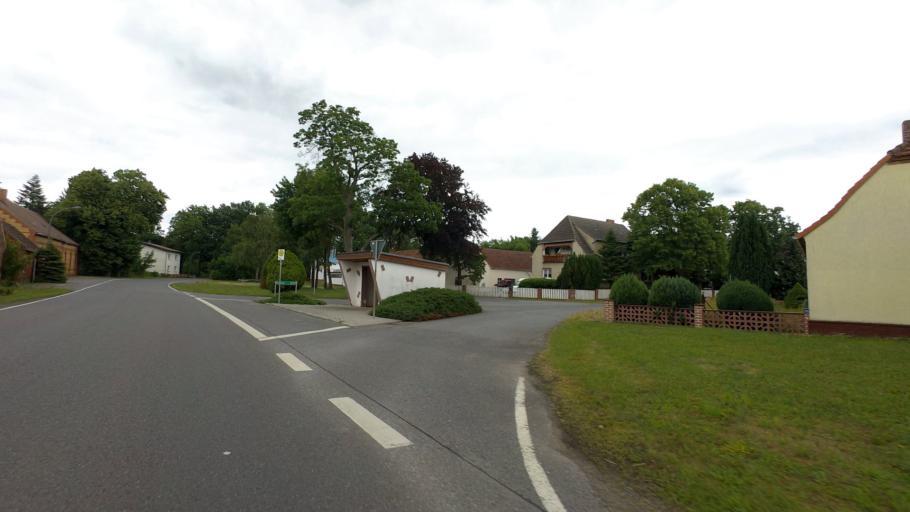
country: DE
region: Brandenburg
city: Crinitz
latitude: 51.7977
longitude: 13.8549
